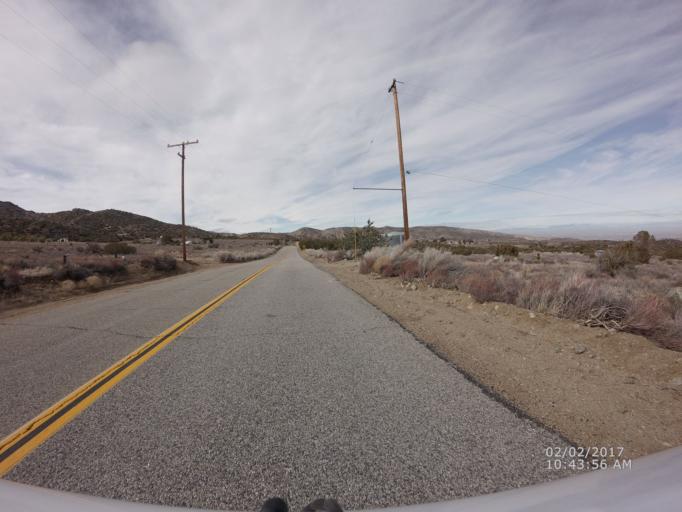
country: US
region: California
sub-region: Los Angeles County
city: Littlerock
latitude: 34.4463
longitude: -117.9445
